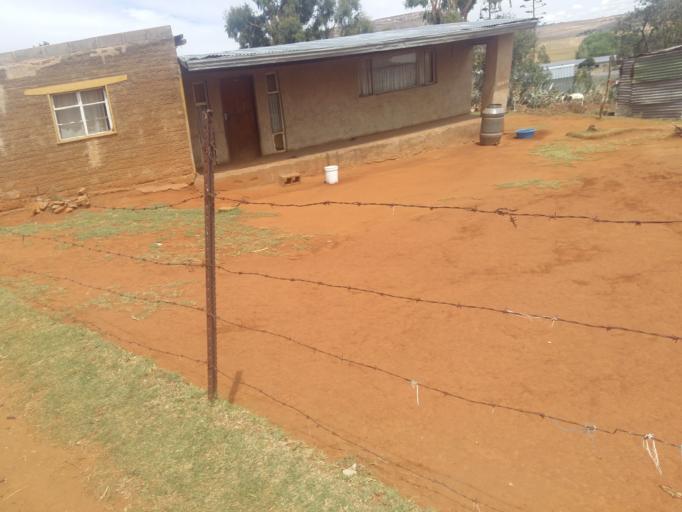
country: LS
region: Mafeteng
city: Mafeteng
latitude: -29.7024
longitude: 27.4341
